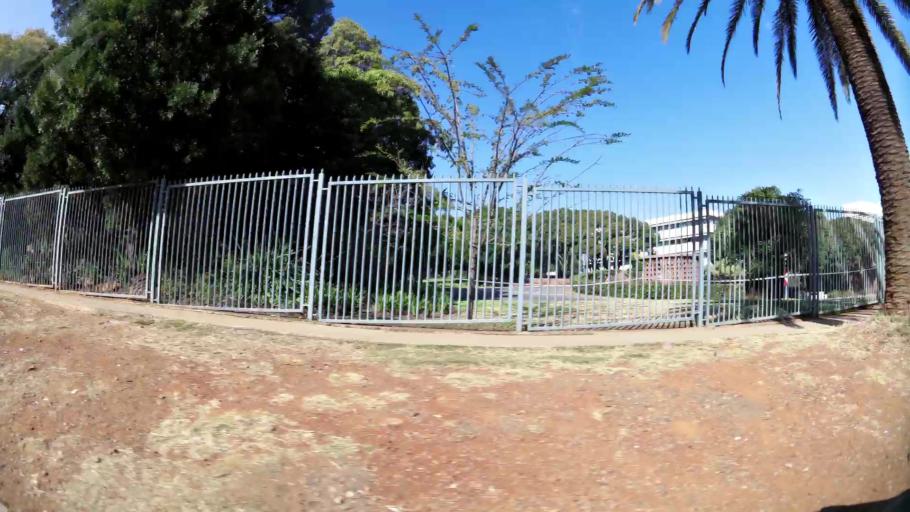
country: ZA
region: Gauteng
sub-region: City of Tshwane Metropolitan Municipality
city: Pretoria
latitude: -25.7545
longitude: 28.2261
